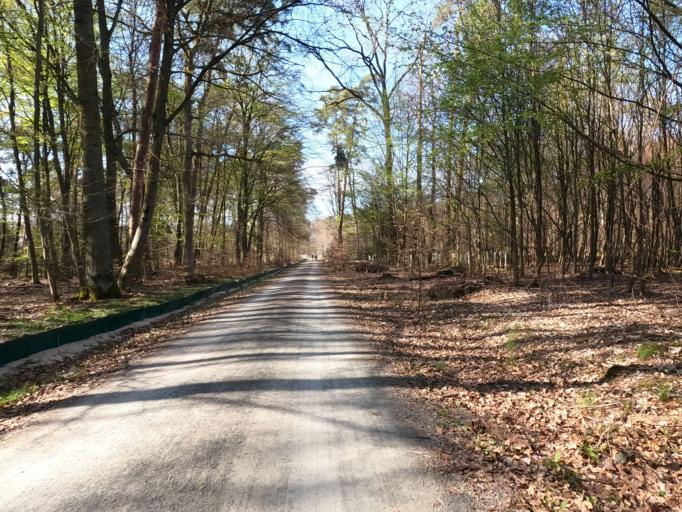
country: DE
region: Hesse
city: Langen
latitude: 50.0098
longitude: 8.6343
